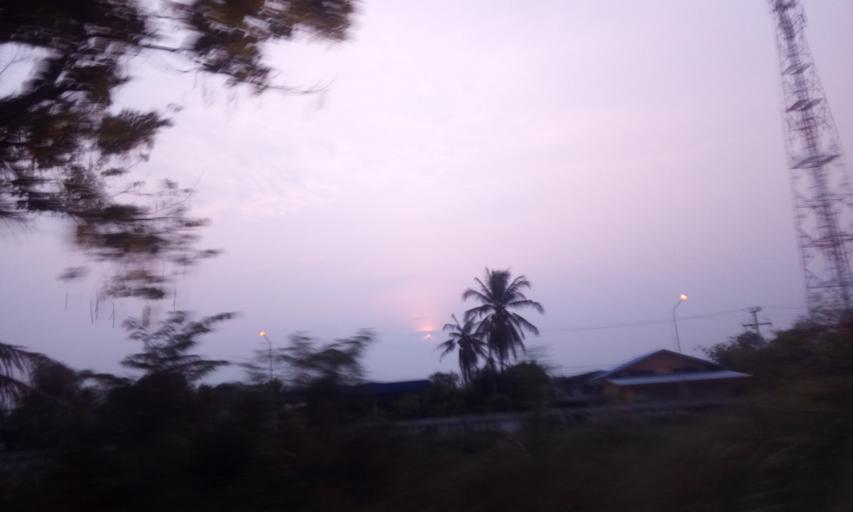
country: TH
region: Pathum Thani
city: Ban Lam Luk Ka
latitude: 14.0237
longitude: 100.8941
